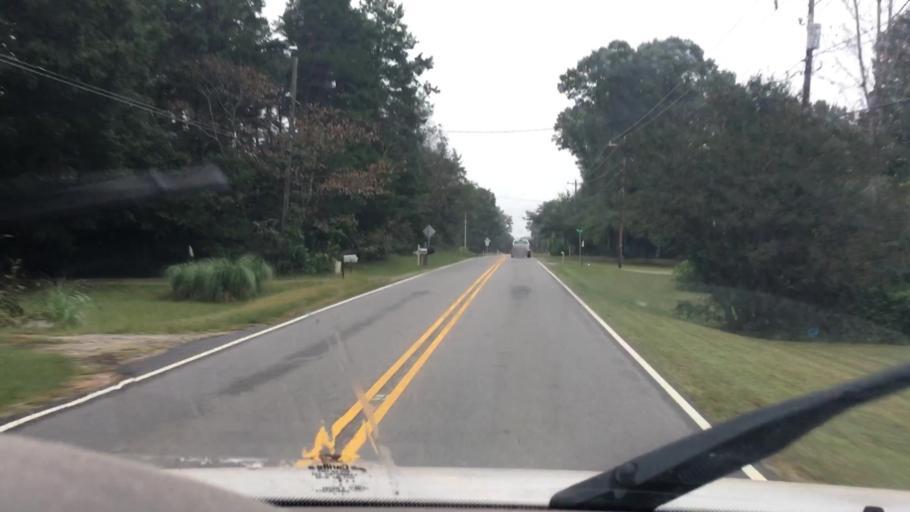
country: US
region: North Carolina
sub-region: Iredell County
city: Mooresville
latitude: 35.6134
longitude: -80.7887
